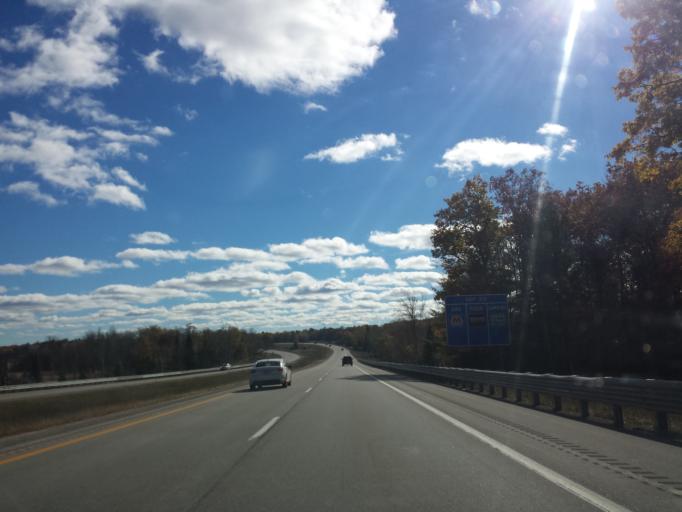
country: US
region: Michigan
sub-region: Cheboygan County
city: Indian River
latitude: 45.4611
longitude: -84.6157
